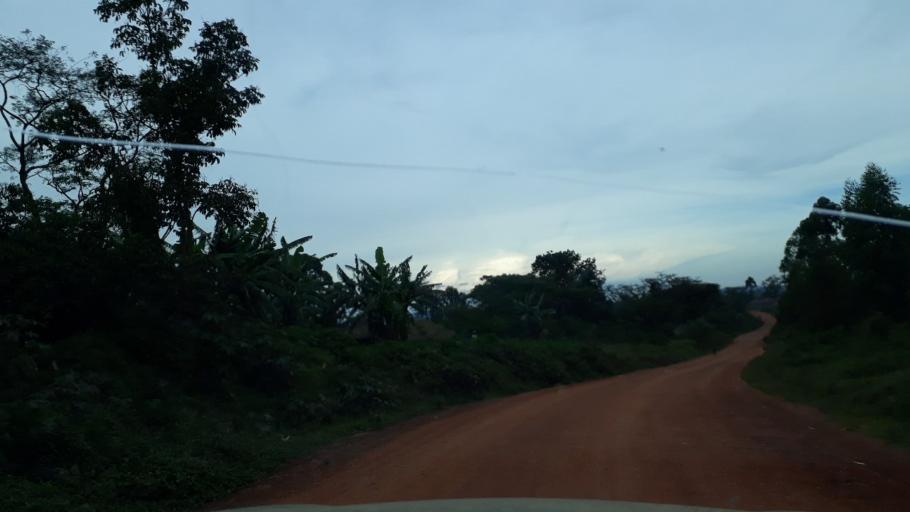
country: UG
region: Northern Region
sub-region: Zombo District
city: Paidha
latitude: 2.2064
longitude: 30.7431
